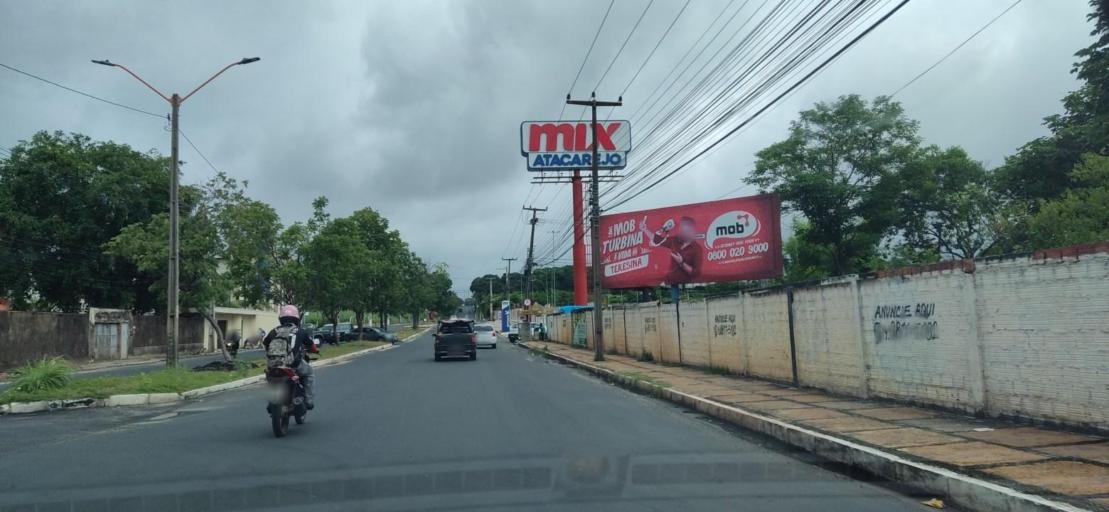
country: BR
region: Piaui
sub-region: Teresina
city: Teresina
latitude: -5.0667
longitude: -42.7491
